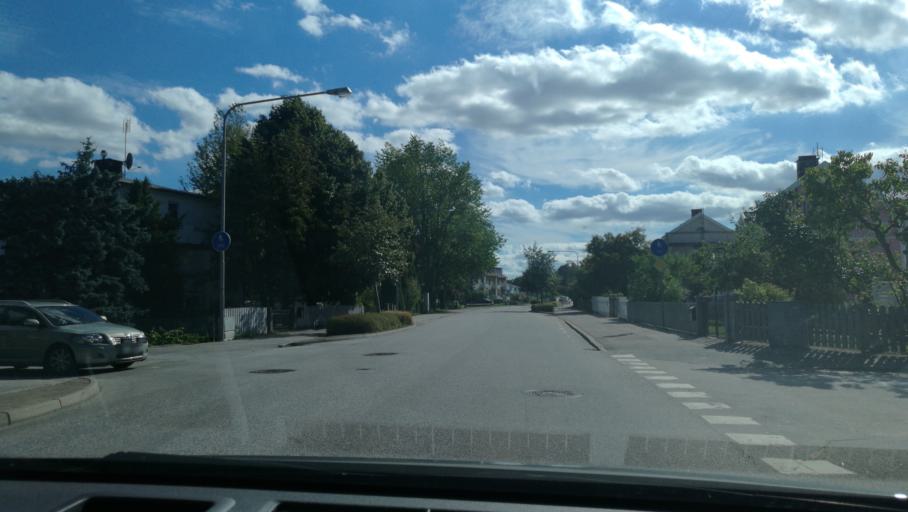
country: SE
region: Vaestra Goetaland
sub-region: Mariestads Kommun
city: Mariestad
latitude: 58.6977
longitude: 13.8375
